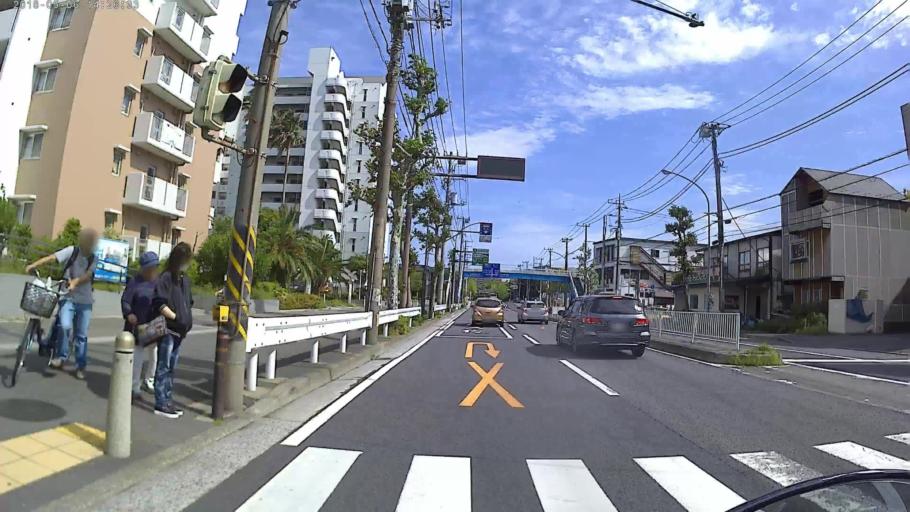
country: JP
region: Kanagawa
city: Yokohama
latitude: 35.4340
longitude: 139.6633
